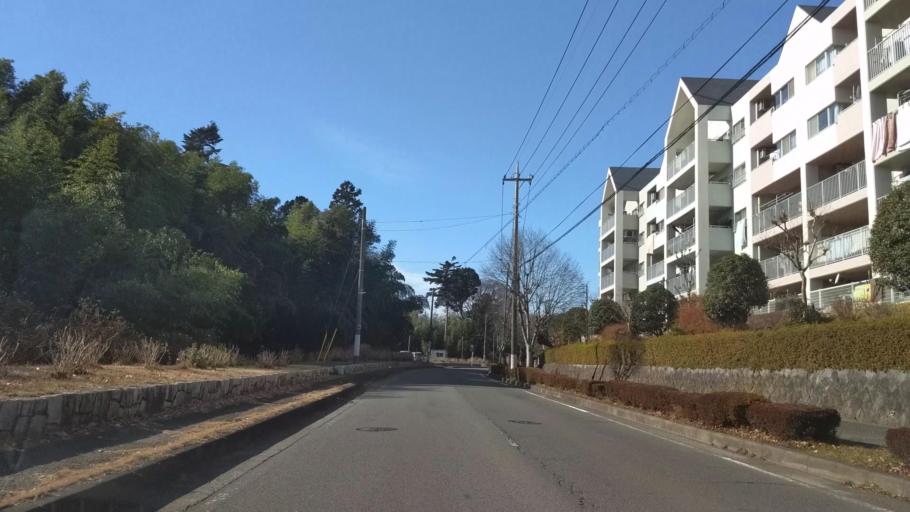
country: JP
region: Kanagawa
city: Hadano
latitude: 35.3526
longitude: 139.2277
